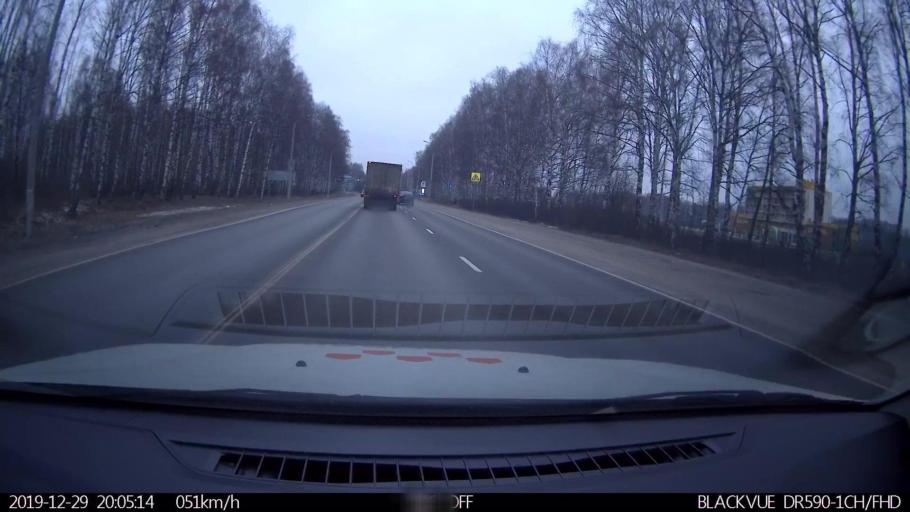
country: RU
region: Nizjnij Novgorod
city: Neklyudovo
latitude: 56.3895
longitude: 44.0112
